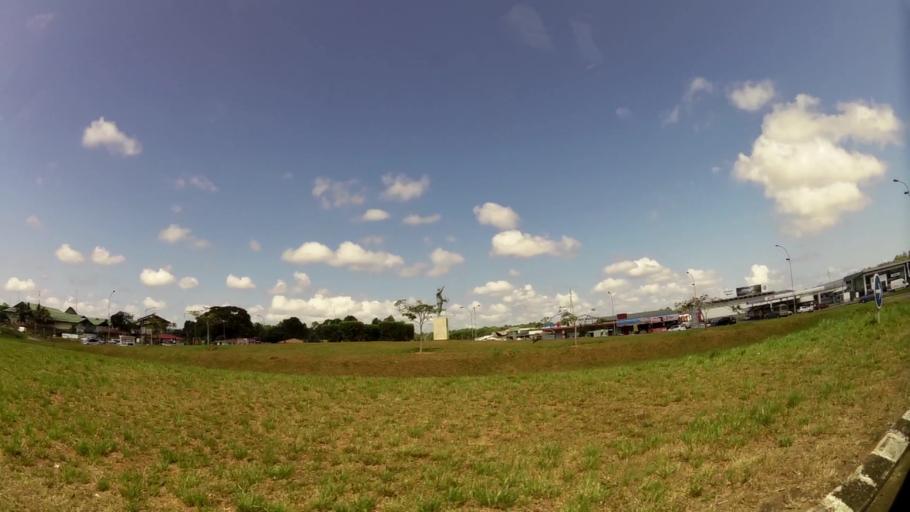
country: GF
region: Guyane
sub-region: Guyane
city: Cayenne
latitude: 4.9248
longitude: -52.3233
